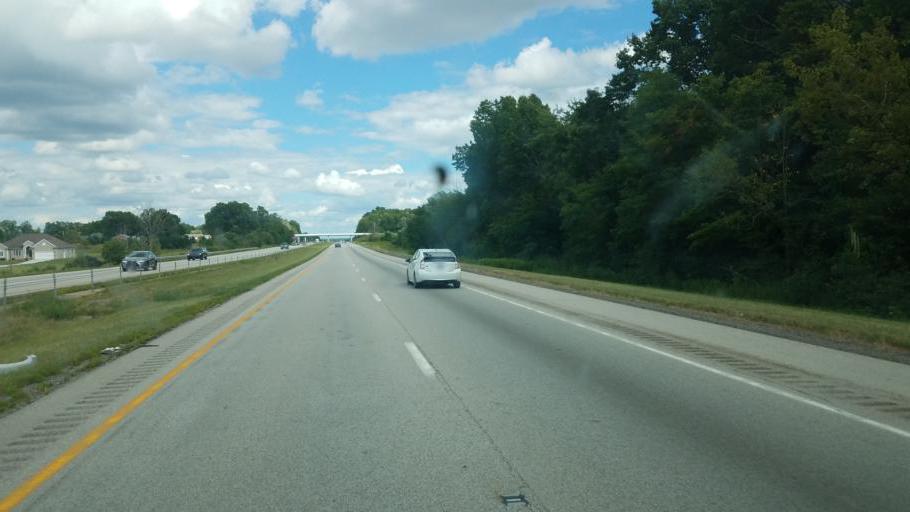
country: US
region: Ohio
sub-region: Medina County
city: Seville
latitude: 41.0319
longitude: -81.8170
